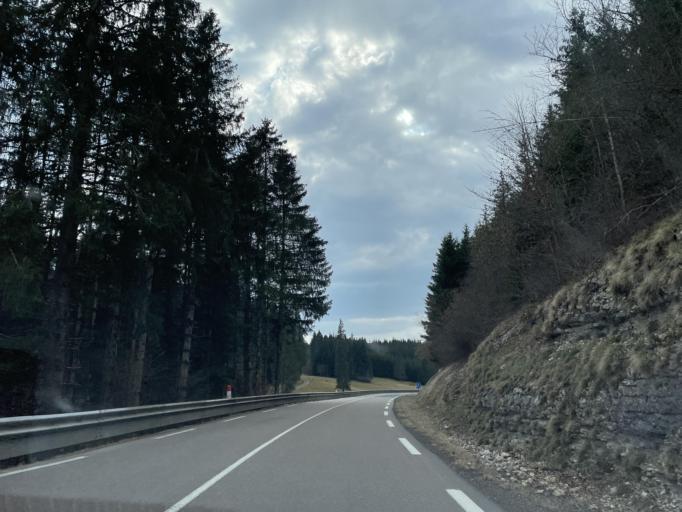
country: FR
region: Franche-Comte
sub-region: Departement du Doubs
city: Gilley
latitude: 47.0317
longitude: 6.5075
